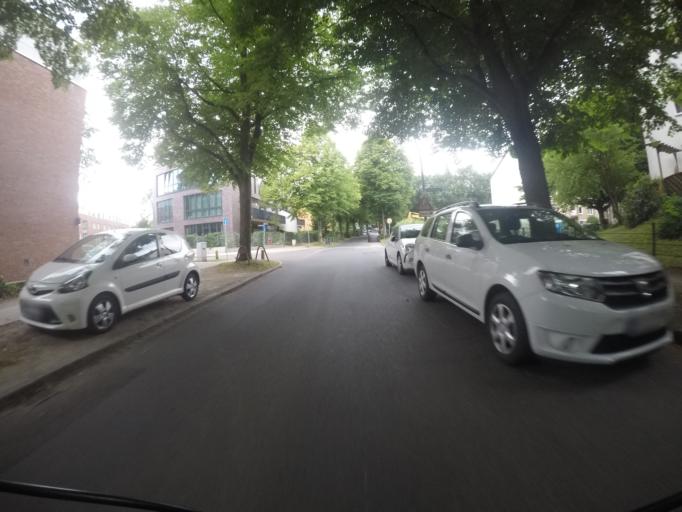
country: DE
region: Hamburg
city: Eidelstedt
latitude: 53.6029
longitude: 9.9042
